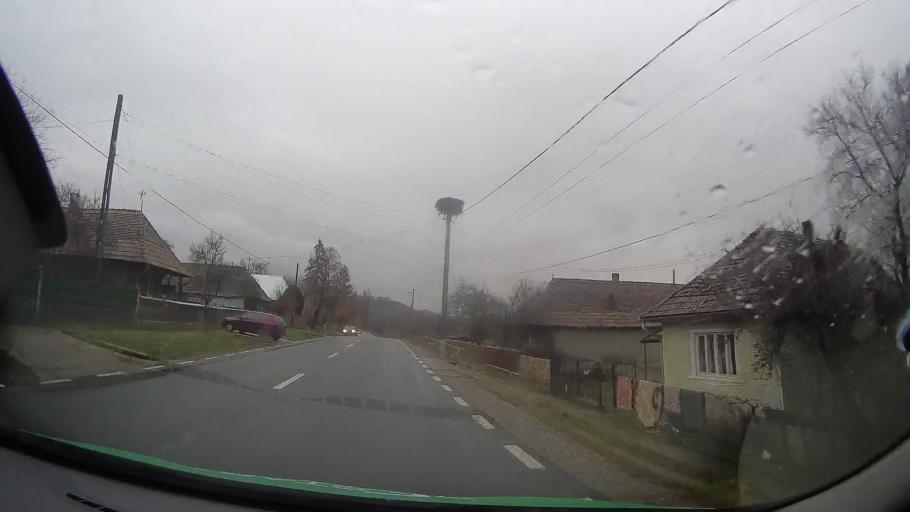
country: RO
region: Bistrita-Nasaud
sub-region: Comuna Galatii Bistritei
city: Galatii Bistritei
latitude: 46.9865
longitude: 24.4258
